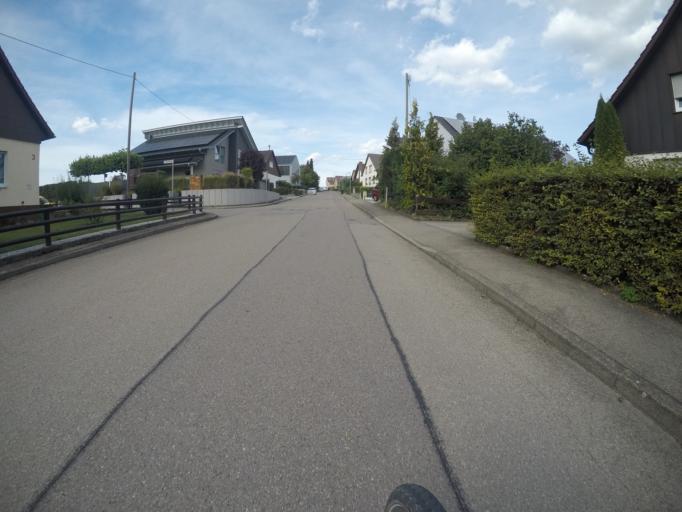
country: DE
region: Baden-Wuerttemberg
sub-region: Regierungsbezirk Stuttgart
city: Gartringen
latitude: 48.6396
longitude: 8.8893
